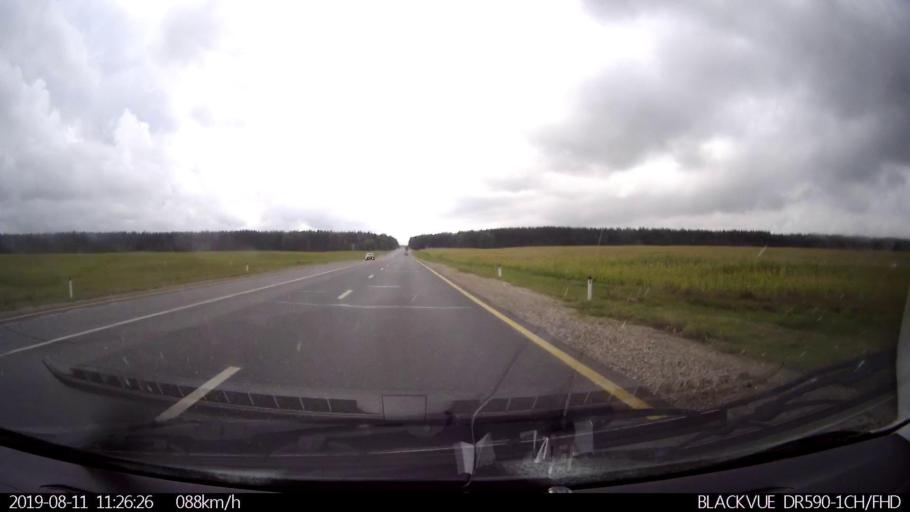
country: RU
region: Ulyanovsk
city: Krasnyy Gulyay
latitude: 54.1053
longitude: 48.2350
